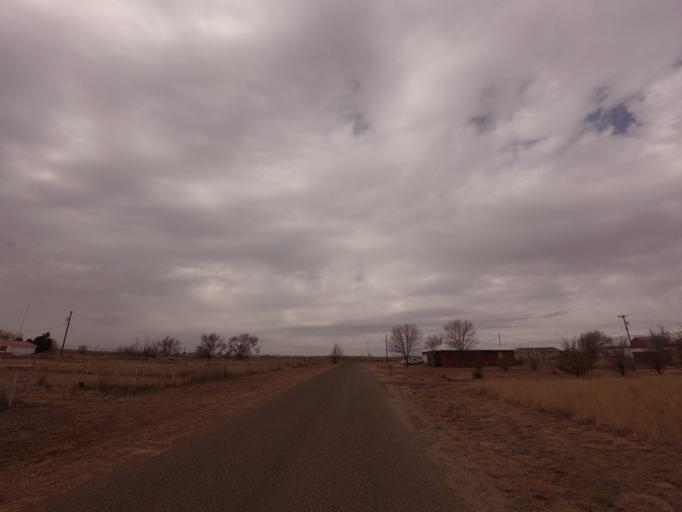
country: US
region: New Mexico
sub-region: Curry County
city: Clovis
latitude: 34.3812
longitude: -103.2039
